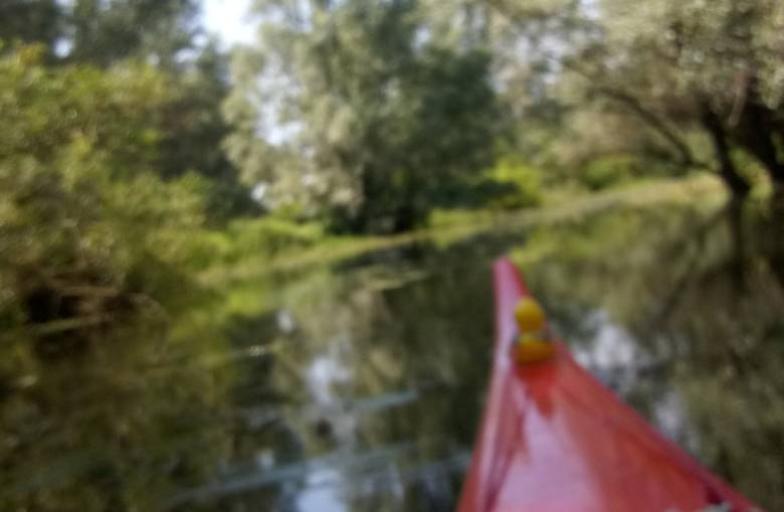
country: NL
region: Gelderland
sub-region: Gemeente Bronckhorst
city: Baak
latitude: 52.0953
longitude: 6.2184
